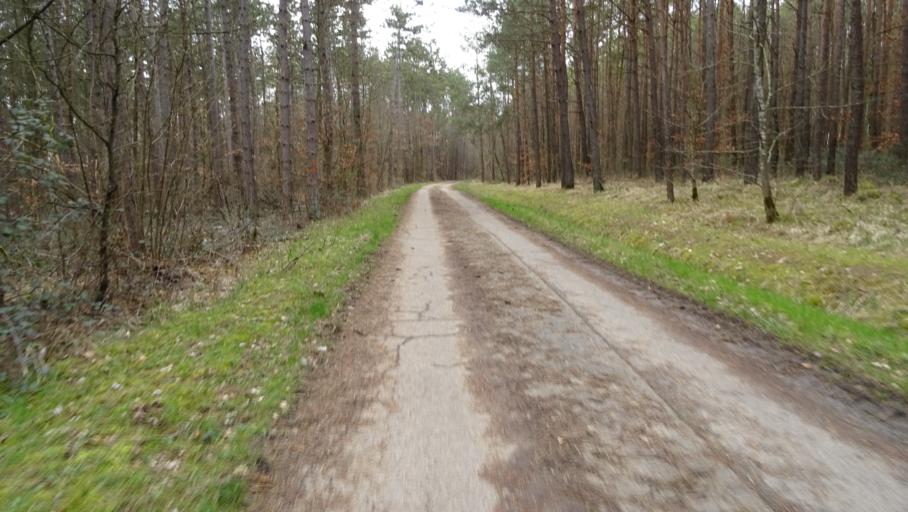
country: DE
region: Baden-Wuerttemberg
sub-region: Karlsruhe Region
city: Seckach
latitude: 49.4346
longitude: 9.2709
